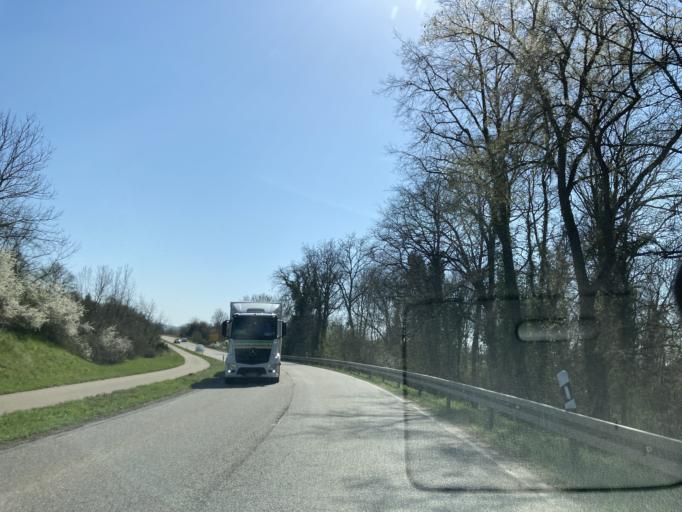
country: DE
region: Baden-Wuerttemberg
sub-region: Freiburg Region
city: Hartheim
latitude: 47.8991
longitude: 7.5963
